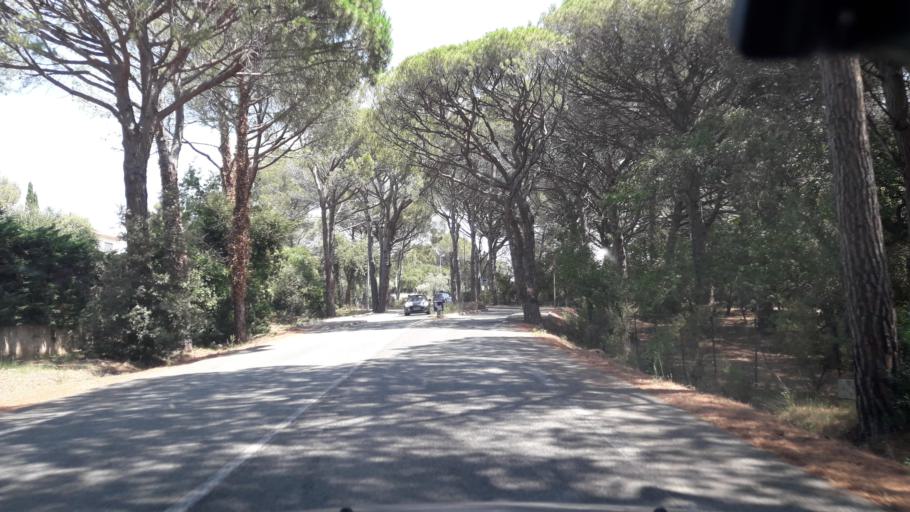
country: FR
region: Provence-Alpes-Cote d'Azur
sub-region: Departement du Var
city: Saint-Raphael
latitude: 43.4471
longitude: 6.8102
